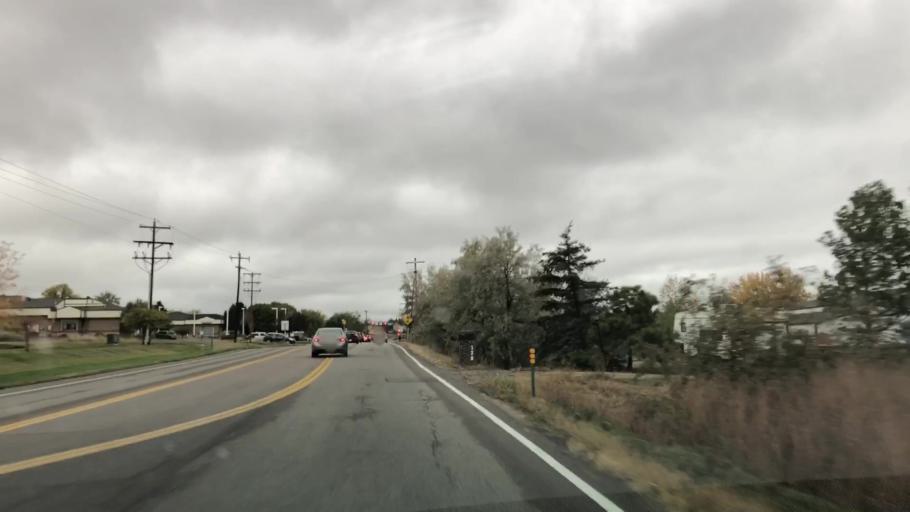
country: US
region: Colorado
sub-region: Larimer County
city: Loveland
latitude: 40.4802
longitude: -105.0744
